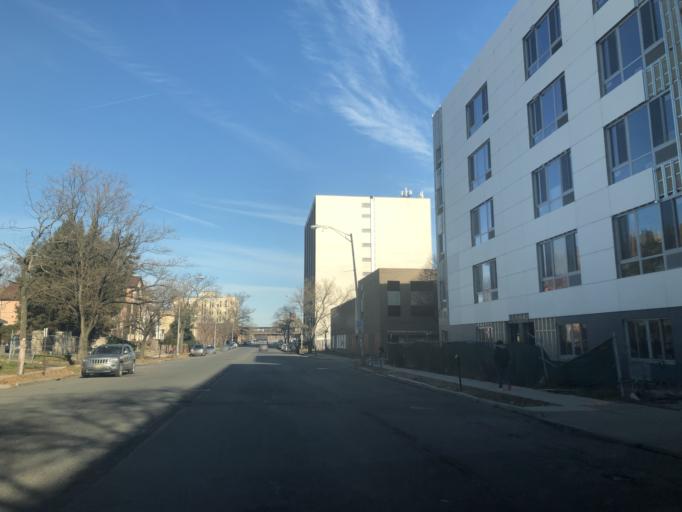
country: US
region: New Jersey
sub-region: Essex County
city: Orange
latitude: 40.7621
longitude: -74.2220
